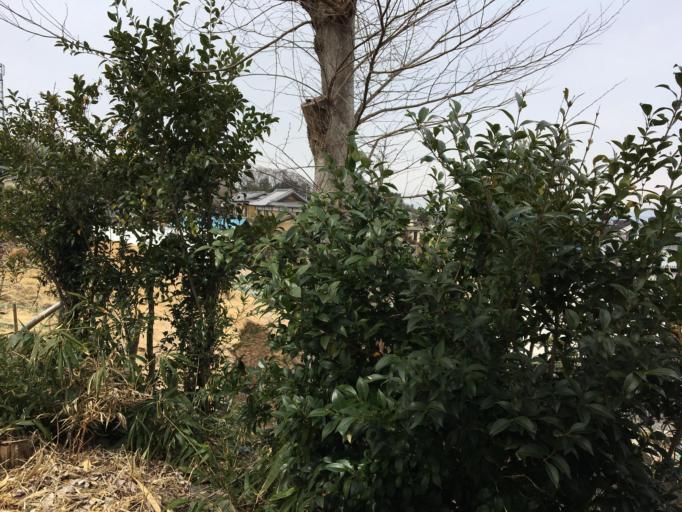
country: JP
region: Saitama
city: Kodamacho-kodamaminami
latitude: 36.1655
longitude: 139.1685
